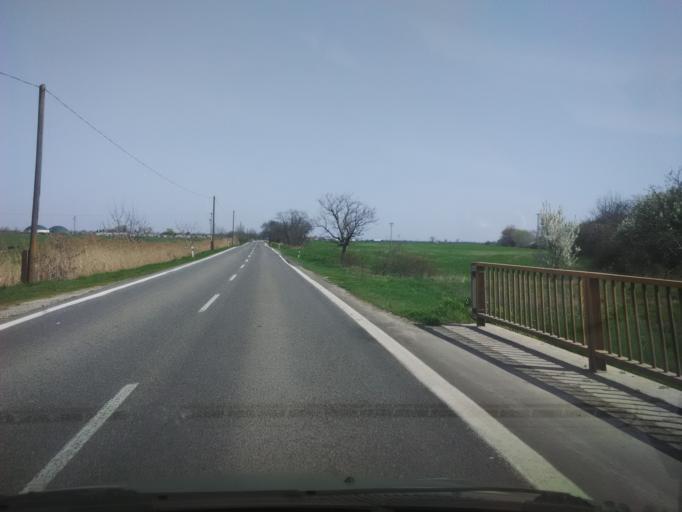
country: SK
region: Nitriansky
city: Sellye
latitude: 48.1513
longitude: 17.9401
